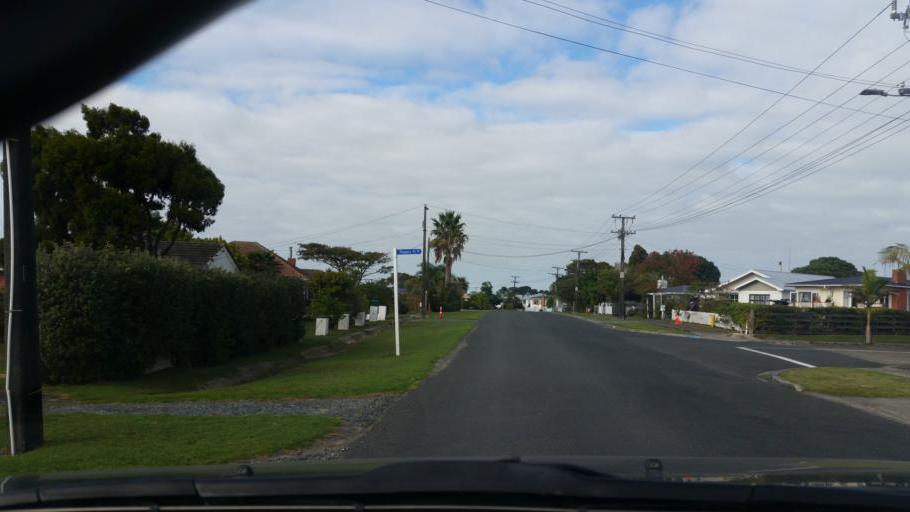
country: NZ
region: Northland
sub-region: Kaipara District
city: Dargaville
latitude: -35.9267
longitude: 173.8690
